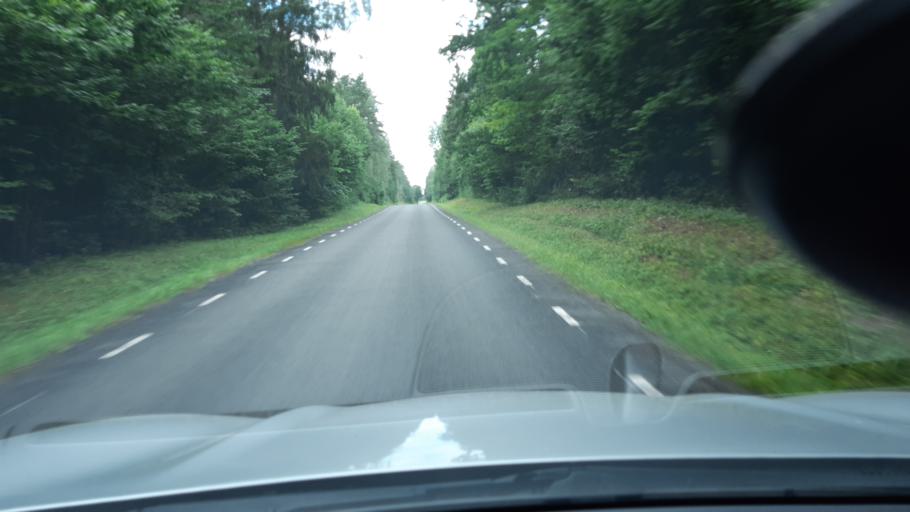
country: EE
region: Raplamaa
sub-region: Jaervakandi vald
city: Jarvakandi
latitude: 58.8811
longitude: 24.7385
